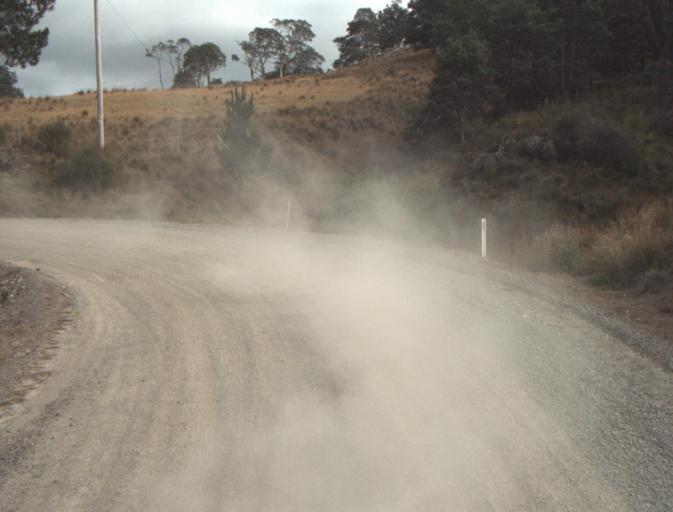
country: AU
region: Tasmania
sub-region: Dorset
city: Scottsdale
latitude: -41.3579
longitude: 147.4605
